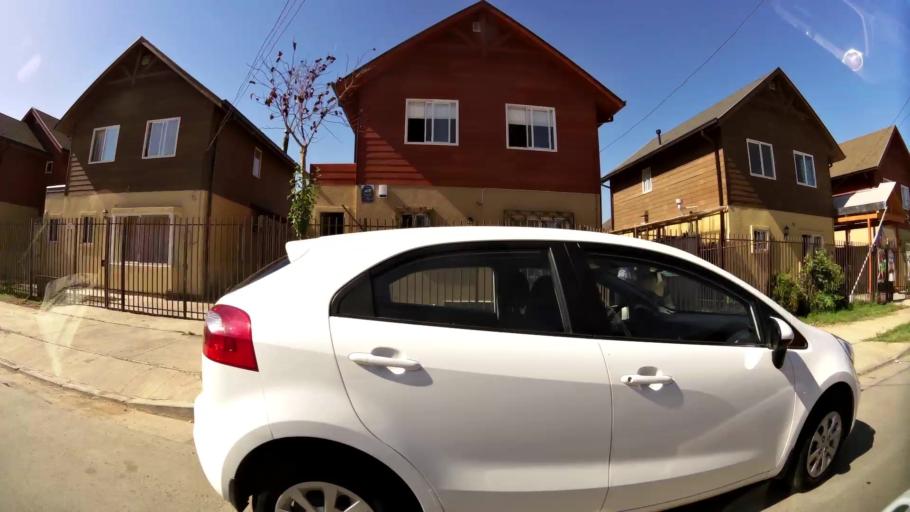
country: CL
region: Maule
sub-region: Provincia de Talca
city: Talca
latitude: -35.4177
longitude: -71.6077
